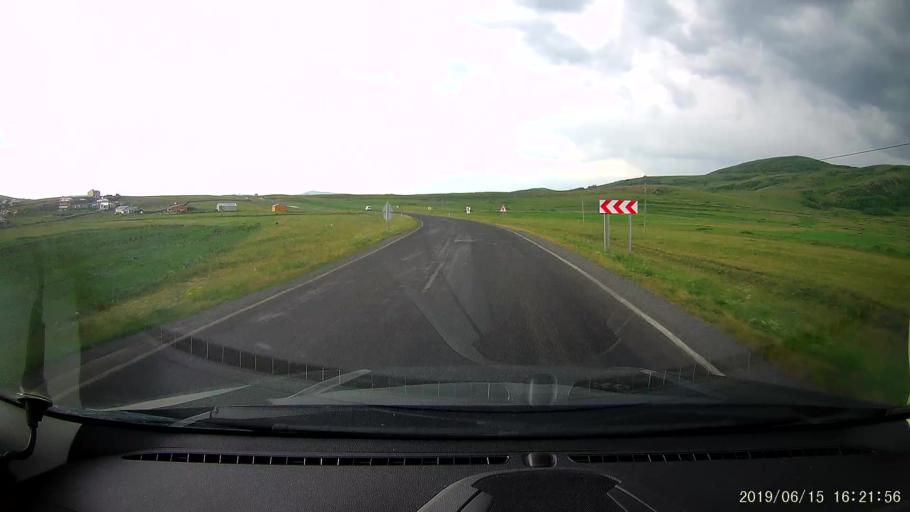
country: TR
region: Ardahan
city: Hanak
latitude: 41.1933
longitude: 42.8458
